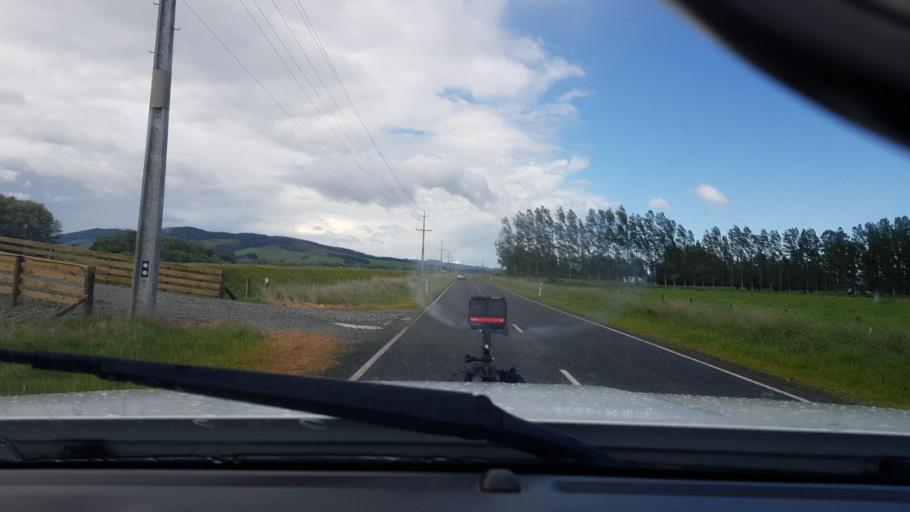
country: NZ
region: Southland
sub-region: Southland District
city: Winton
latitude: -45.8069
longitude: 168.3767
